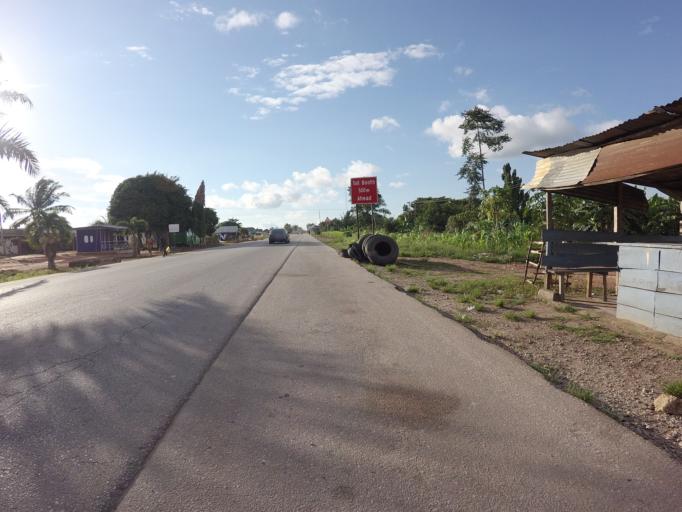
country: GH
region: Ashanti
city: Tafo
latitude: 6.9158
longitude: -1.6589
